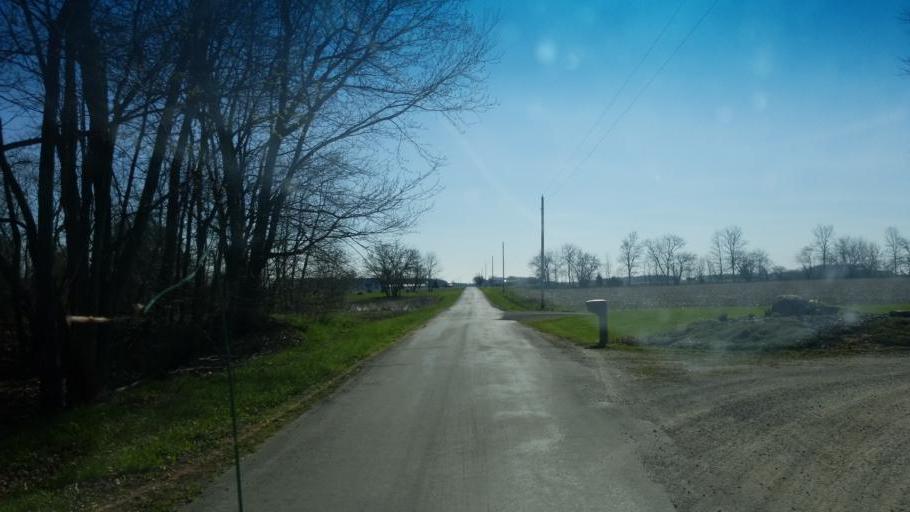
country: US
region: Ohio
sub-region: Hardin County
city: Forest
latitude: 40.7088
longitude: -83.4849
